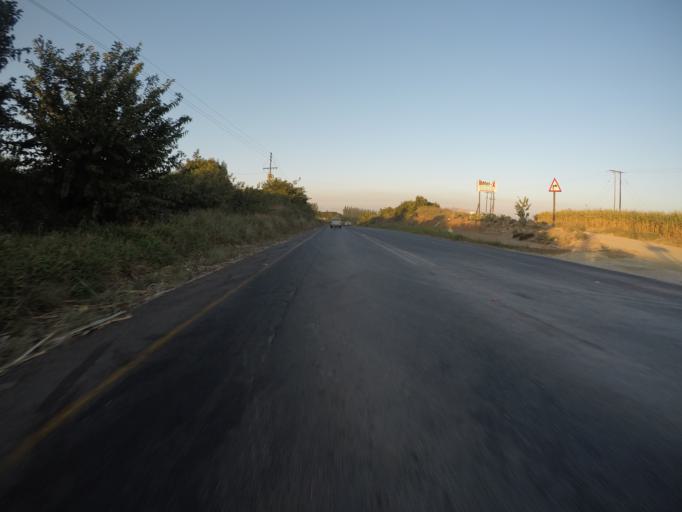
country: ZA
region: KwaZulu-Natal
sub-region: uThungulu District Municipality
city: Empangeni
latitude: -28.8099
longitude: 31.8915
